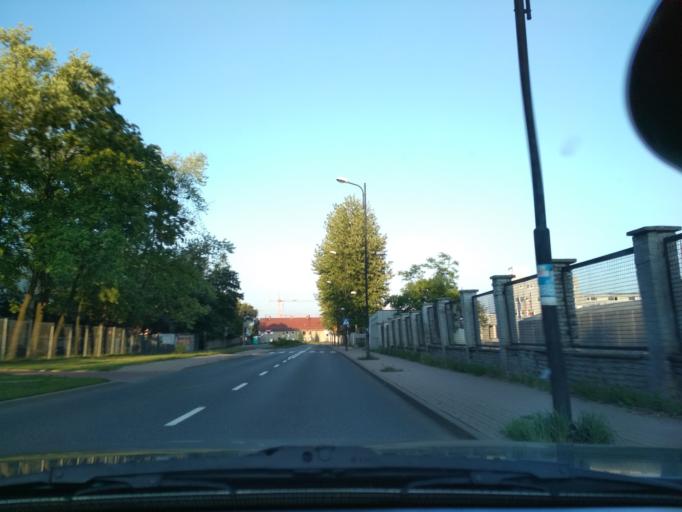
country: PL
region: Silesian Voivodeship
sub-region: Gliwice
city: Gliwice
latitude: 50.2749
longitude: 18.6709
